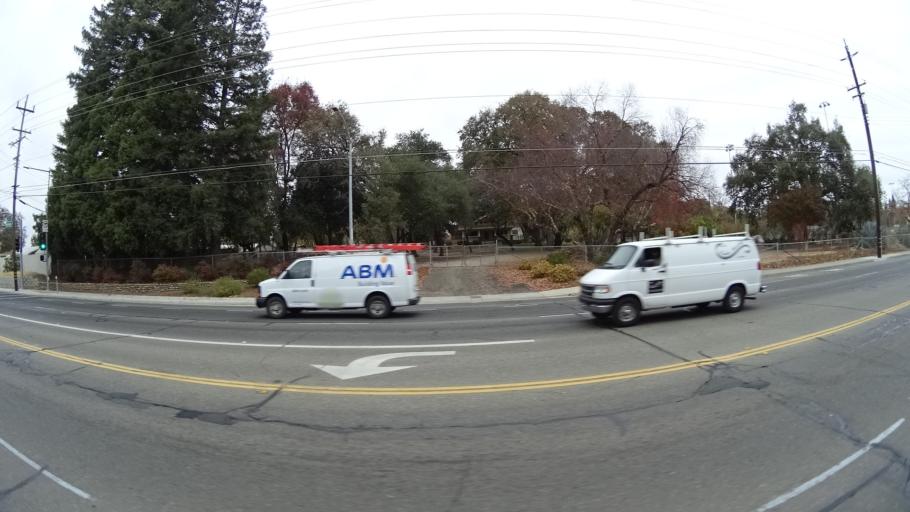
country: US
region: California
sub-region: Sacramento County
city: Citrus Heights
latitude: 38.7074
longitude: -121.2995
